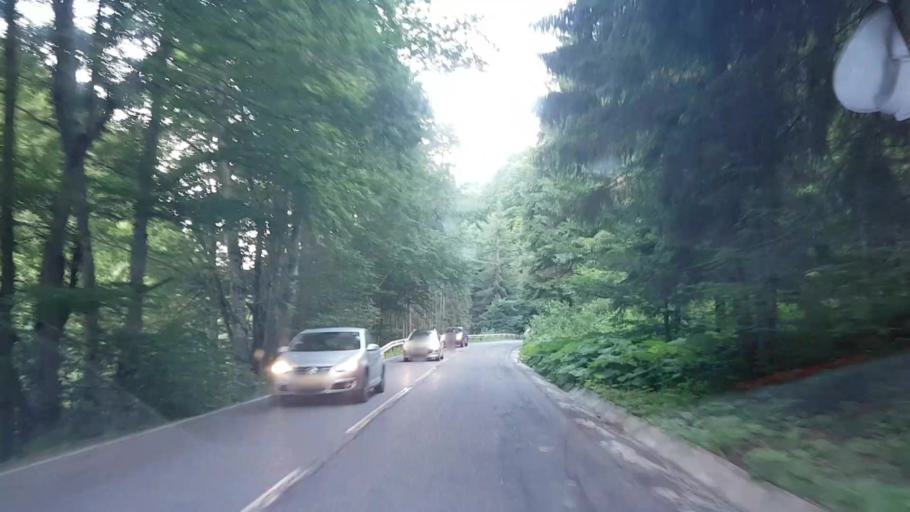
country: RO
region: Harghita
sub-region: Comuna Praid
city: Ocna de Sus
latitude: 46.6012
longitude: 25.2392
